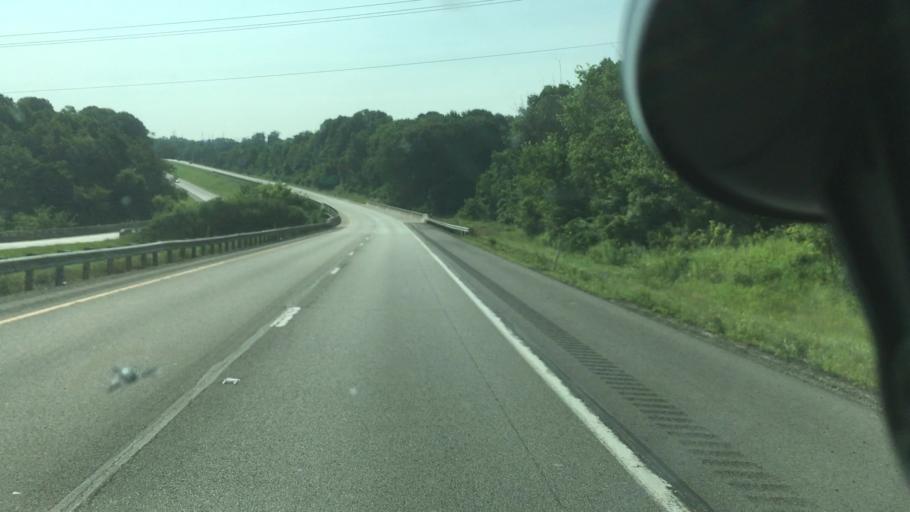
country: US
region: Pennsylvania
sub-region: Lawrence County
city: New Castle
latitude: 40.9692
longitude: -80.3394
